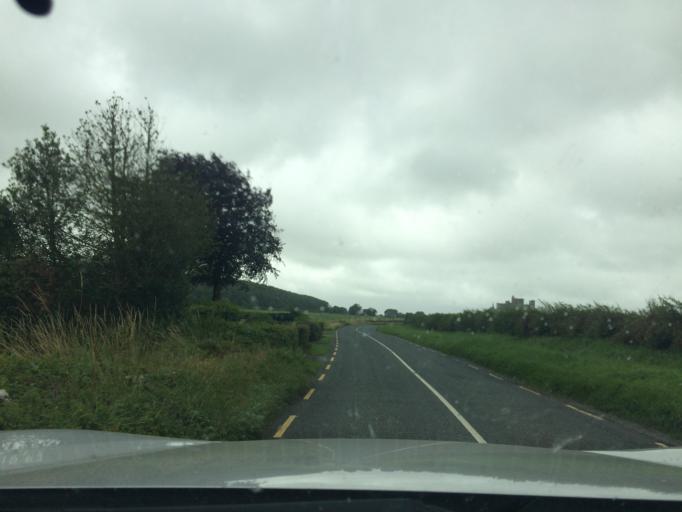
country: IE
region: Munster
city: Cashel
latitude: 52.5295
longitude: -7.8892
